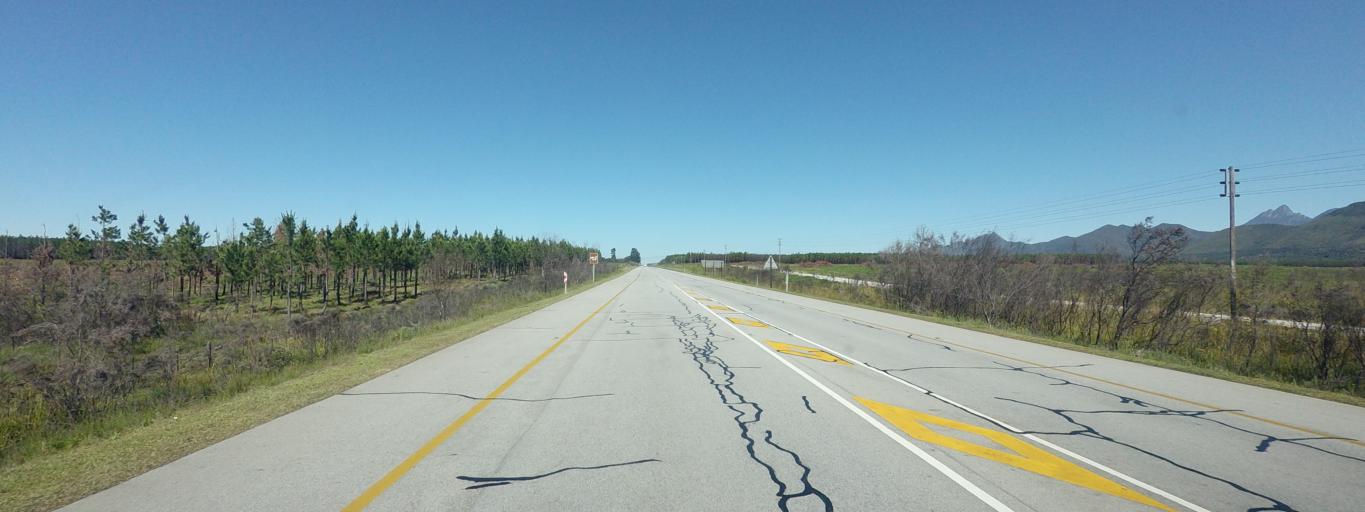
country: ZA
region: Eastern Cape
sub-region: Cacadu District Municipality
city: Kareedouw
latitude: -33.9714
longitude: 23.8369
